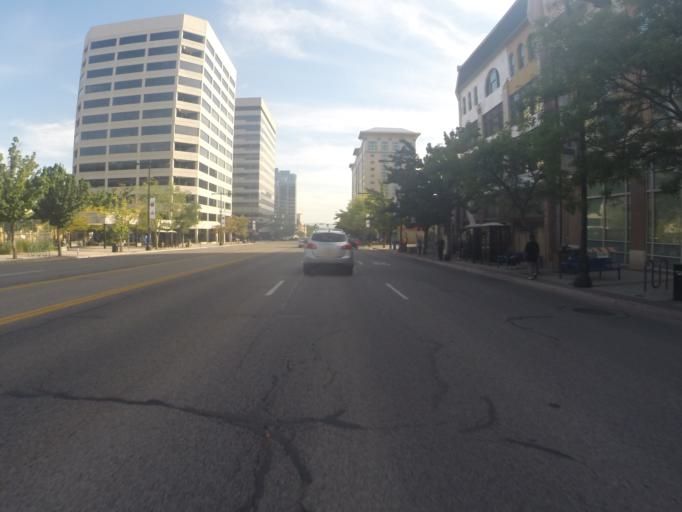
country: US
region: Utah
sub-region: Salt Lake County
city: Salt Lake City
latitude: 40.7662
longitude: -111.8883
